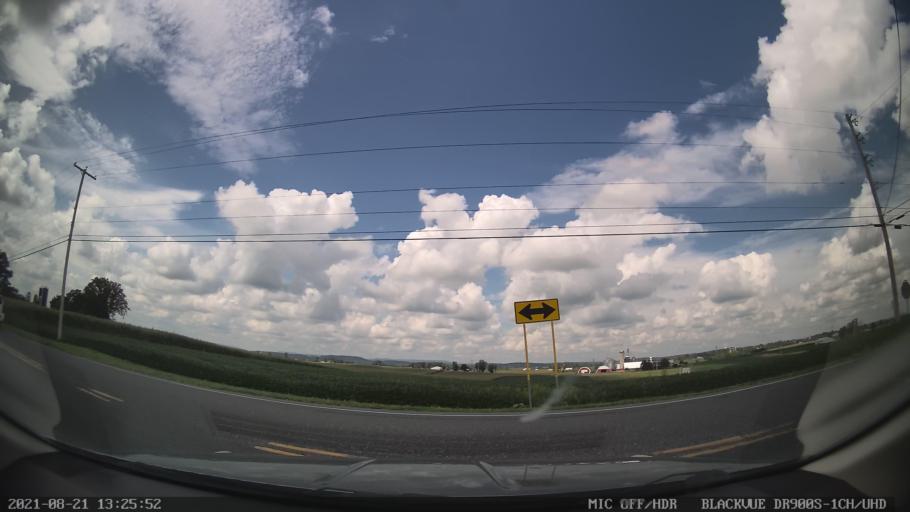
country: US
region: Pennsylvania
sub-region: Berks County
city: Fleetwood
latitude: 40.4767
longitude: -75.7860
